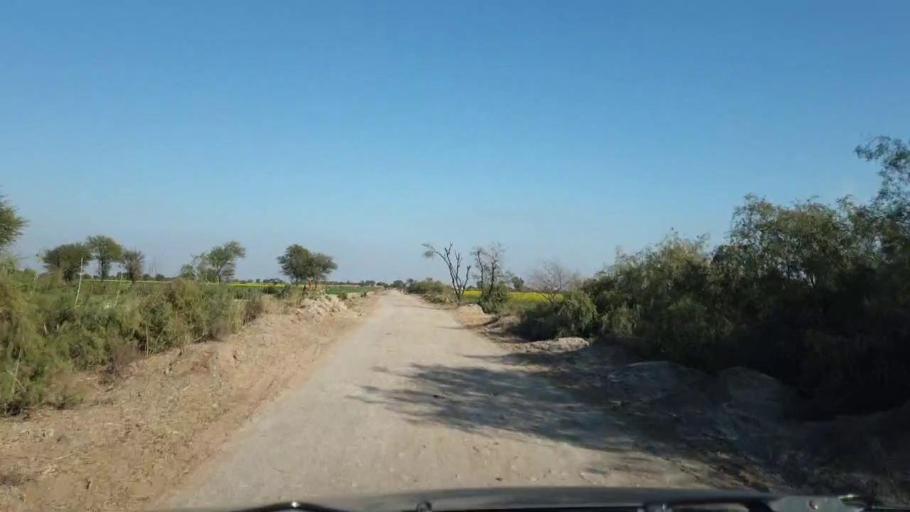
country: PK
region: Sindh
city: Khadro
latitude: 26.2034
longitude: 68.7534
